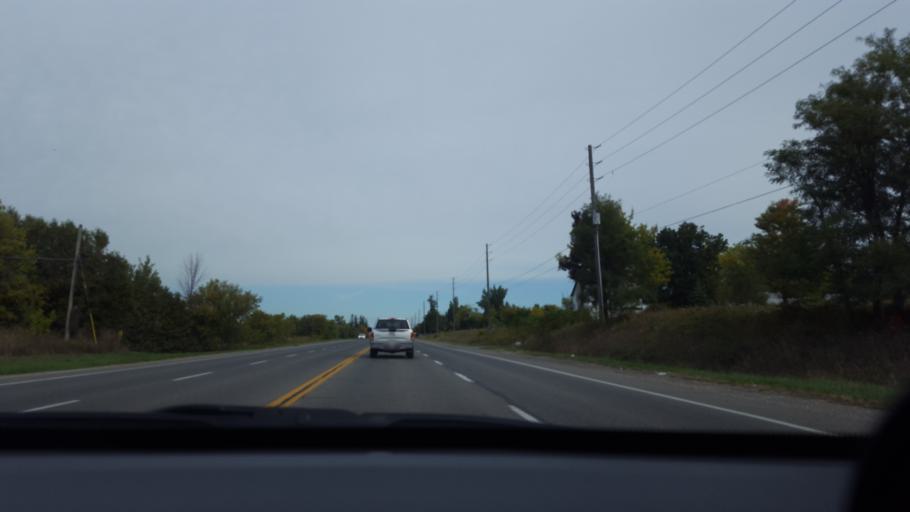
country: CA
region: Ontario
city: Vaughan
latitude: 43.8803
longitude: -79.5183
